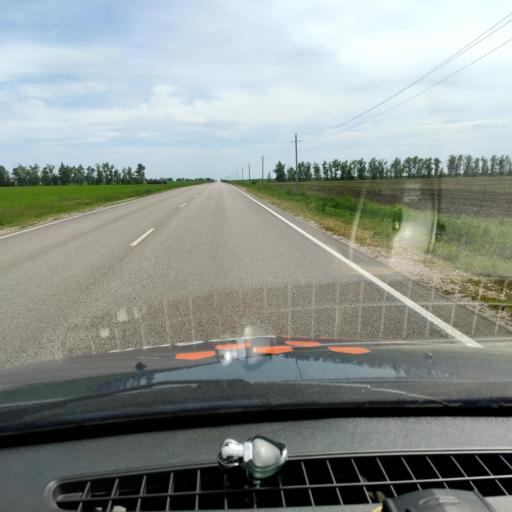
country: RU
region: Voronezj
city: Novaya Usman'
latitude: 51.5685
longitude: 39.3756
